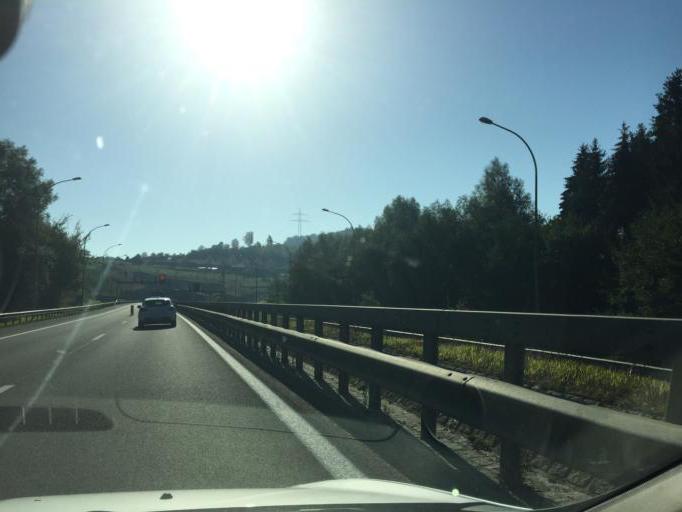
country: LU
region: Luxembourg
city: Rollingen
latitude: 49.7334
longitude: 6.1017
